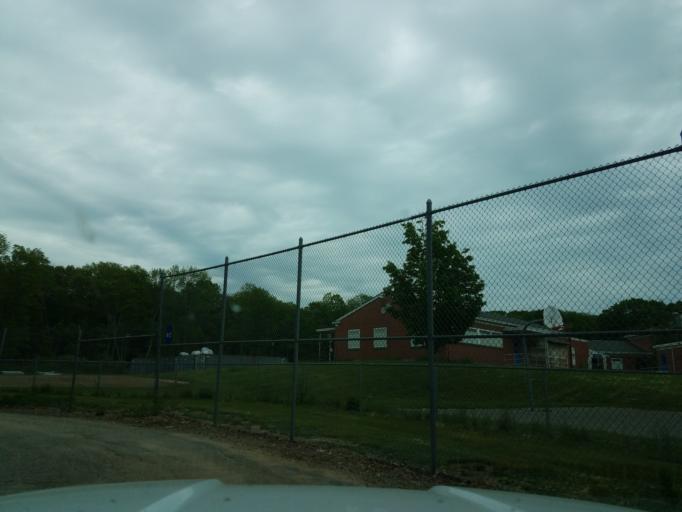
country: US
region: Connecticut
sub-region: Tolland County
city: South Coventry
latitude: 41.8145
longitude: -72.2969
